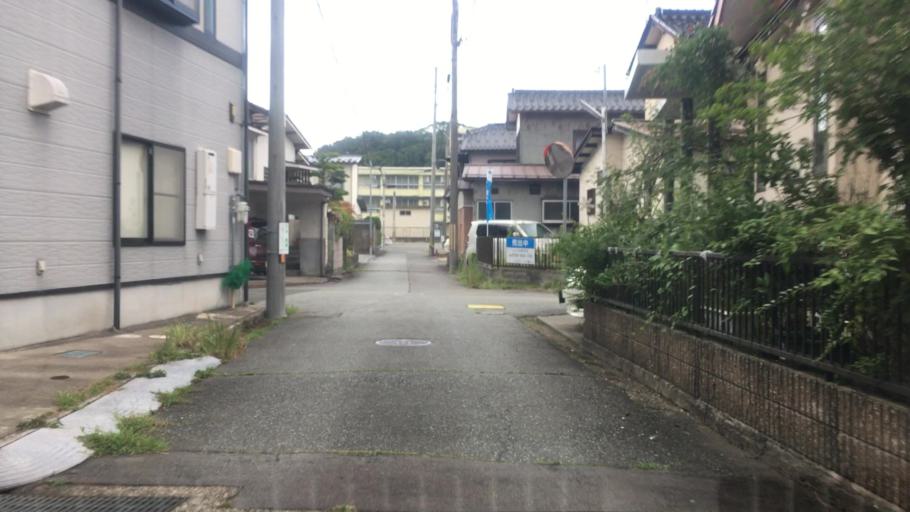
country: JP
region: Hyogo
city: Toyooka
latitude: 35.5362
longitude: 134.8206
